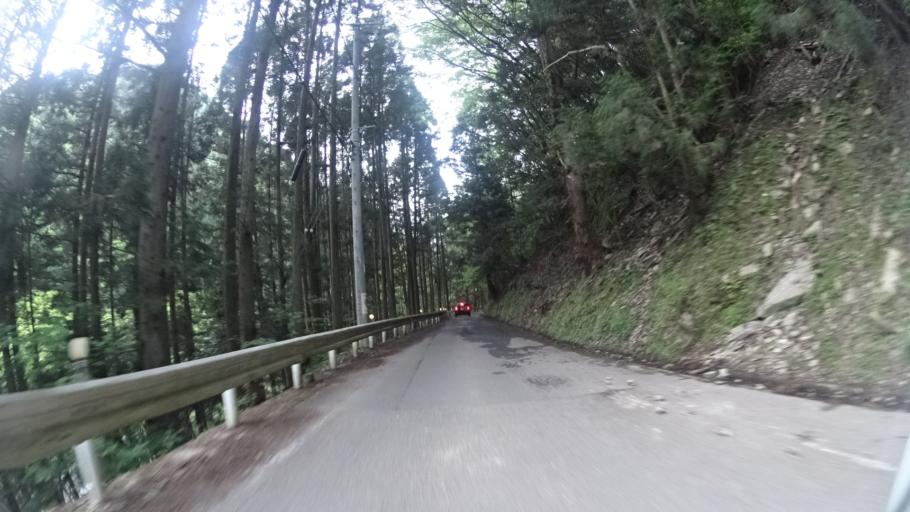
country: JP
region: Tokushima
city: Ikedacho
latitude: 33.9481
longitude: 133.8040
